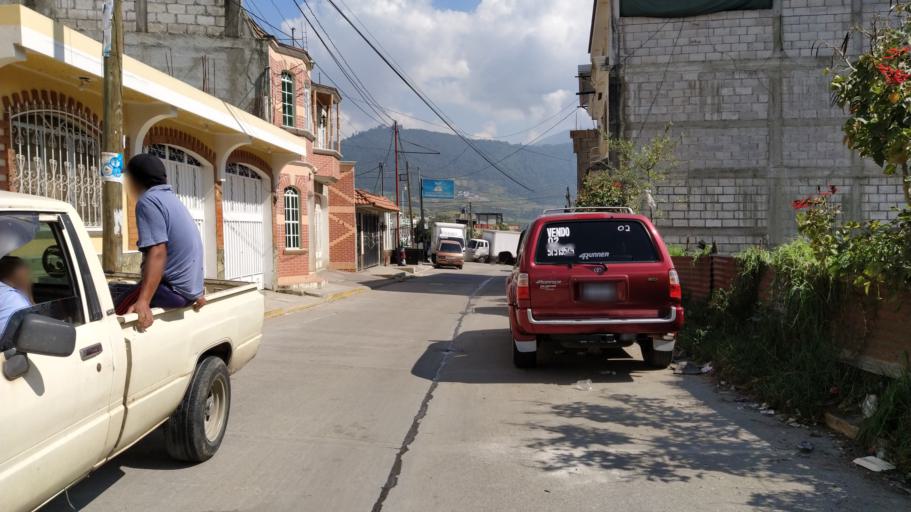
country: GT
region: Quetzaltenango
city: Almolonga
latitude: 14.8156
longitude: -91.4924
